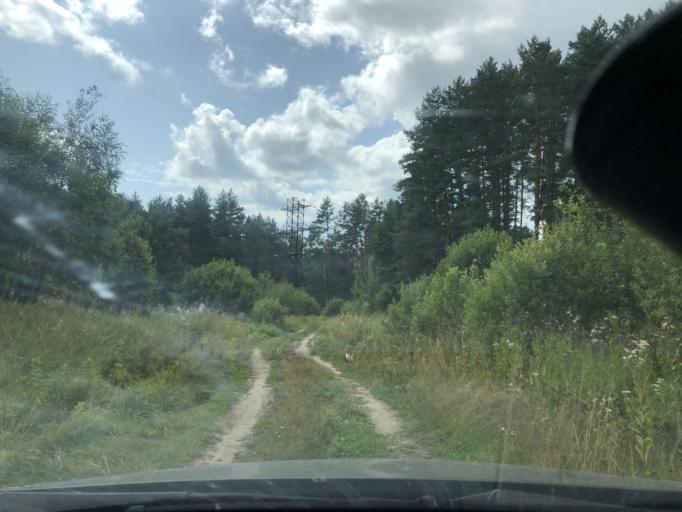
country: RU
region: Kaluga
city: Yukhnov
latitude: 54.7360
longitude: 35.1399
